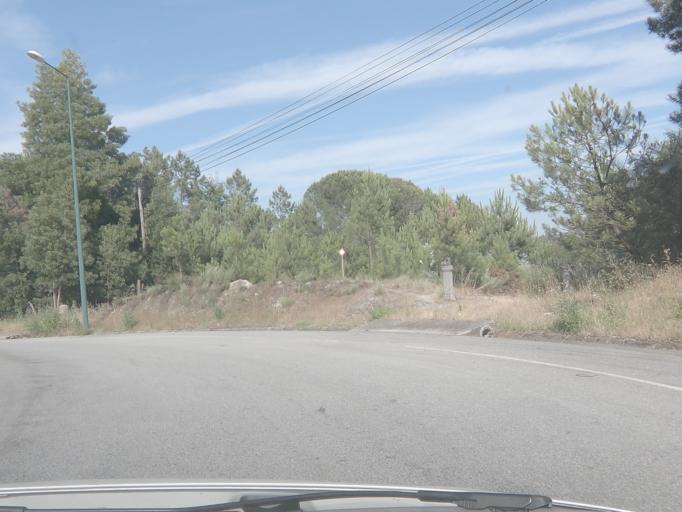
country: PT
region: Viseu
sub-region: Viseu
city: Viseu
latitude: 40.6300
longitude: -7.9360
